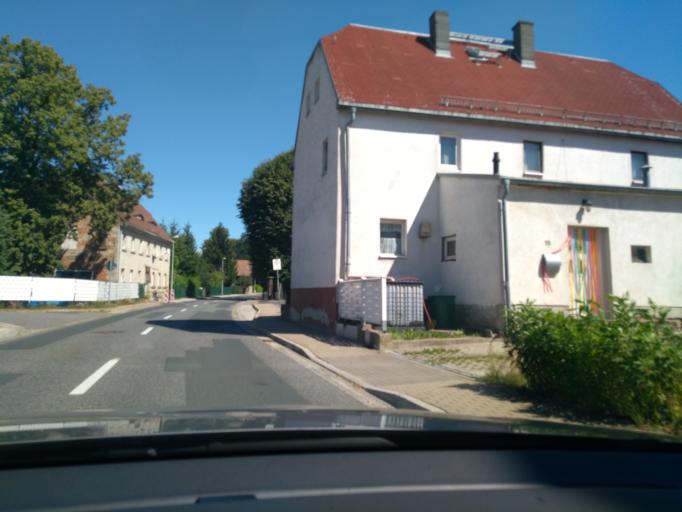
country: DE
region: Saxony
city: Grossrohrsdorf
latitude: 51.1423
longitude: 14.0408
